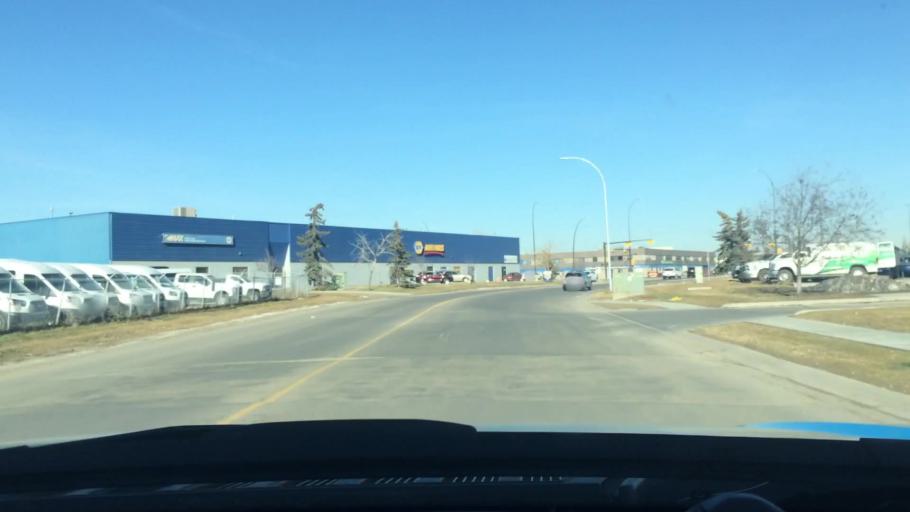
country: CA
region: Alberta
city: Calgary
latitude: 51.0755
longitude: -114.0045
